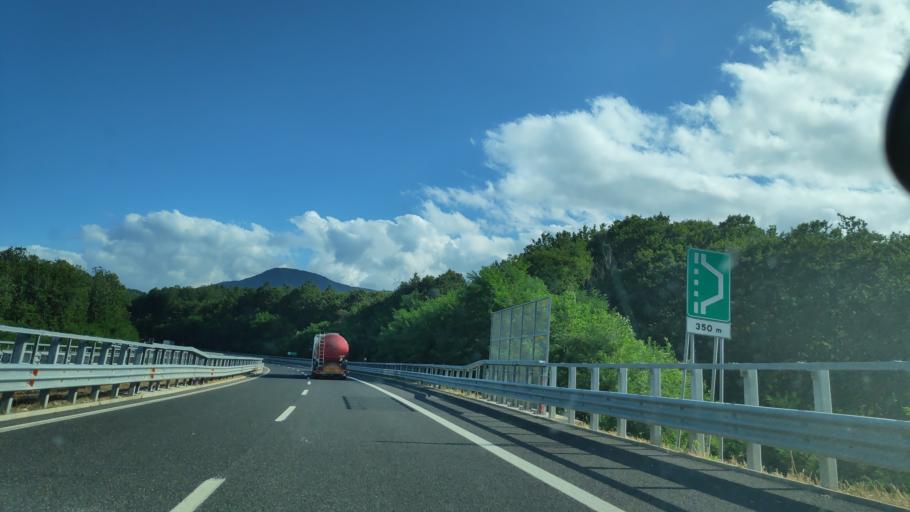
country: IT
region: Campania
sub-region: Provincia di Salerno
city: Casalbuono
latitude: 40.2403
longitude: 15.6597
